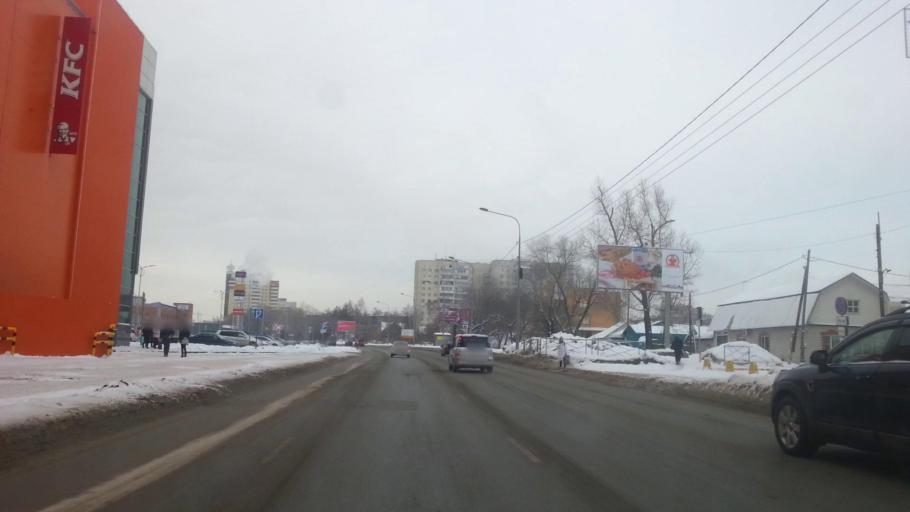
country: RU
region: Altai Krai
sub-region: Gorod Barnaulskiy
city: Barnaul
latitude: 53.3419
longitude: 83.7525
